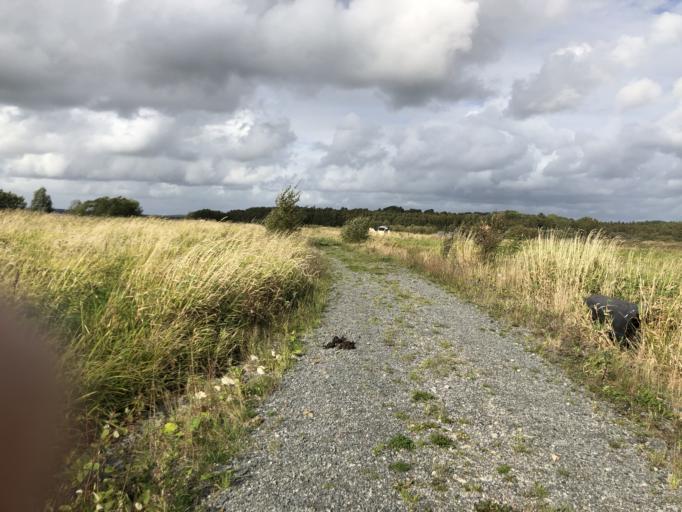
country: SE
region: Vaestra Goetaland
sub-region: Goteborg
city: Majorna
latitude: 57.7637
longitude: 11.8746
